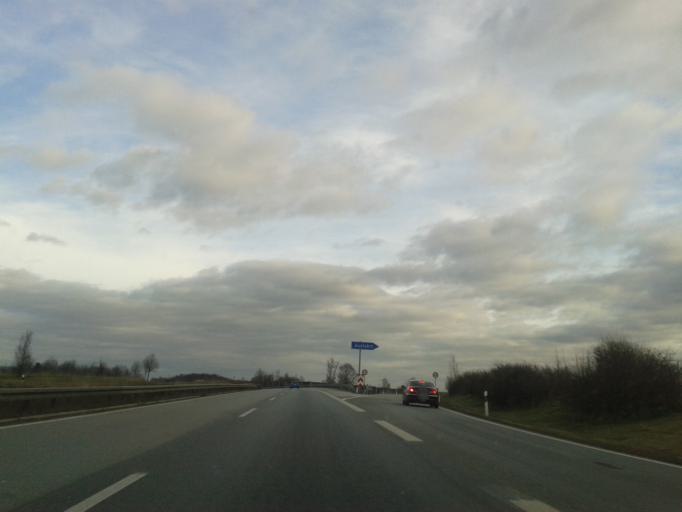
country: DE
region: Saxony
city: Bautzen
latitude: 51.1877
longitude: 14.4084
